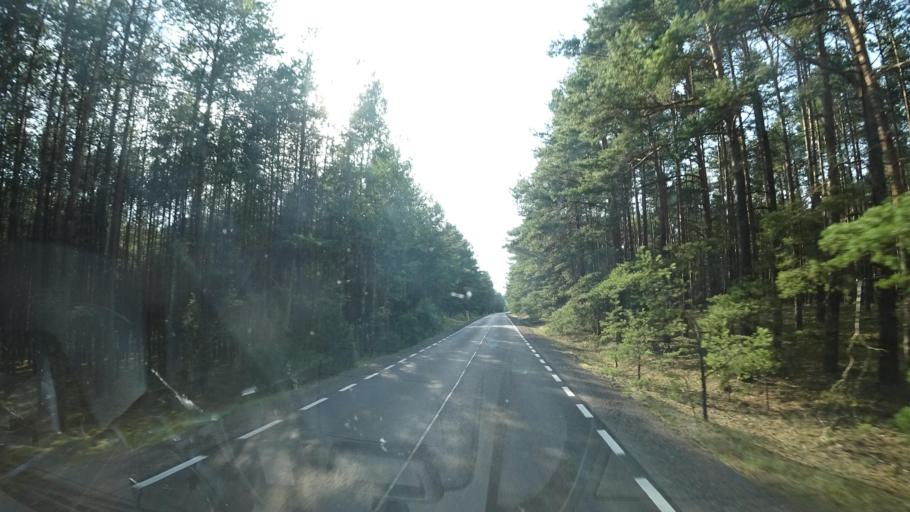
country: PL
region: Pomeranian Voivodeship
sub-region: Powiat chojnicki
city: Chojnice
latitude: 53.8594
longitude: 17.5332
